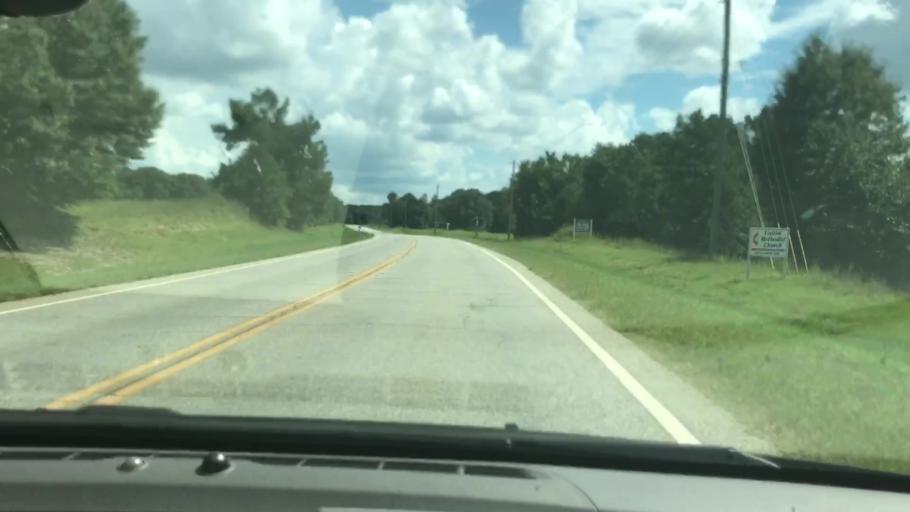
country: US
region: Georgia
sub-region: Clay County
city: Fort Gaines
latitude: 31.6525
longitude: -85.0472
